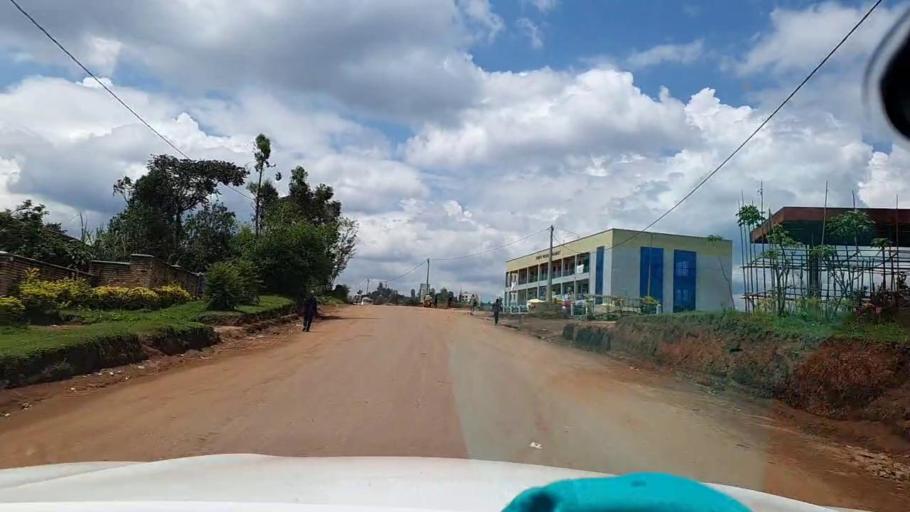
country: RW
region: Southern Province
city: Nzega
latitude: -2.6480
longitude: 29.5615
